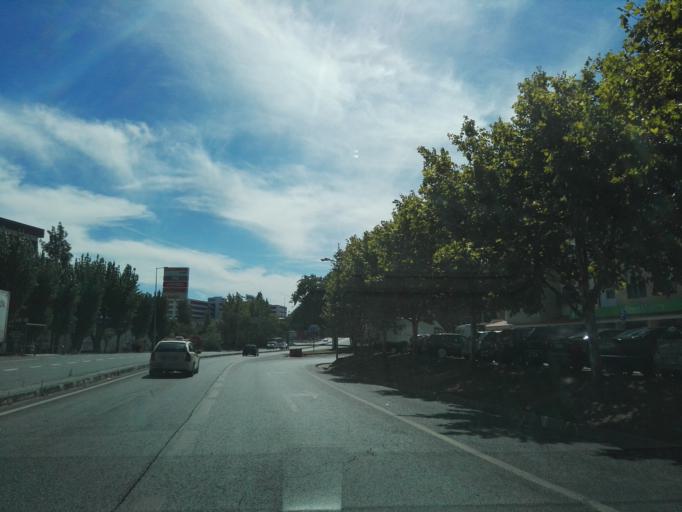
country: PT
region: Lisbon
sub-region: Vila Franca de Xira
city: Sobralinho
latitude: 38.8923
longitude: -9.0423
